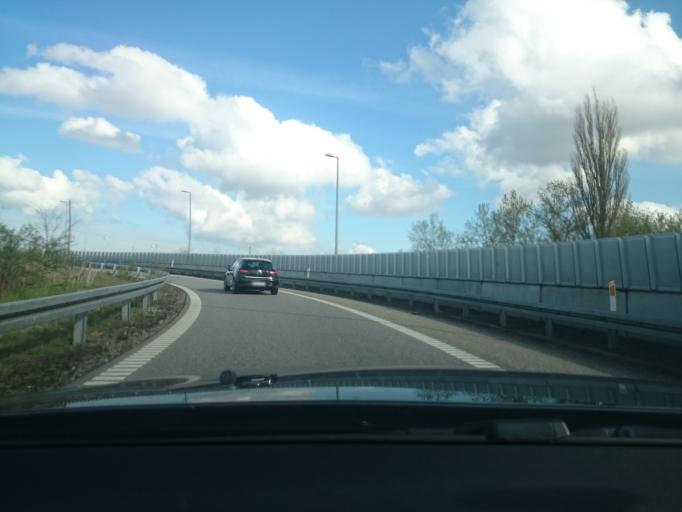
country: DK
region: Capital Region
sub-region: Herlev Kommune
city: Herlev
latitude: 55.7391
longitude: 12.4578
